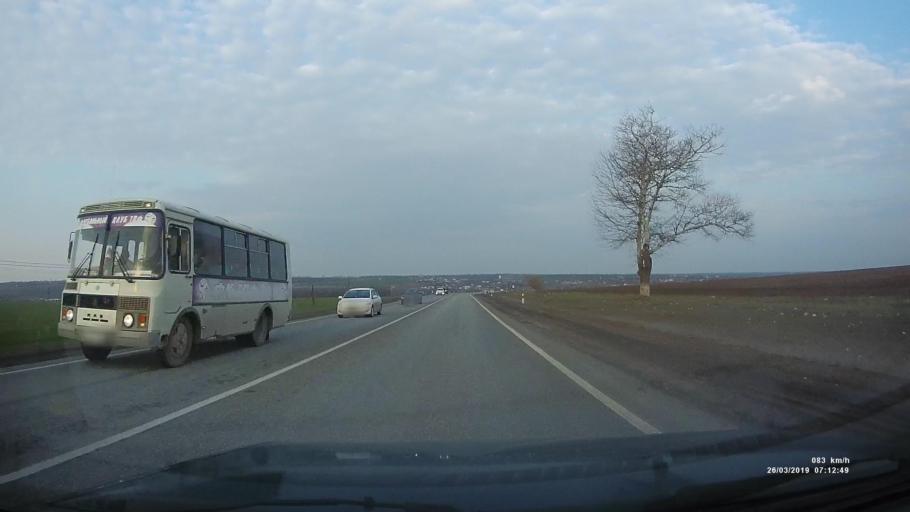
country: RU
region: Rostov
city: Primorka
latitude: 47.3201
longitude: 39.0453
